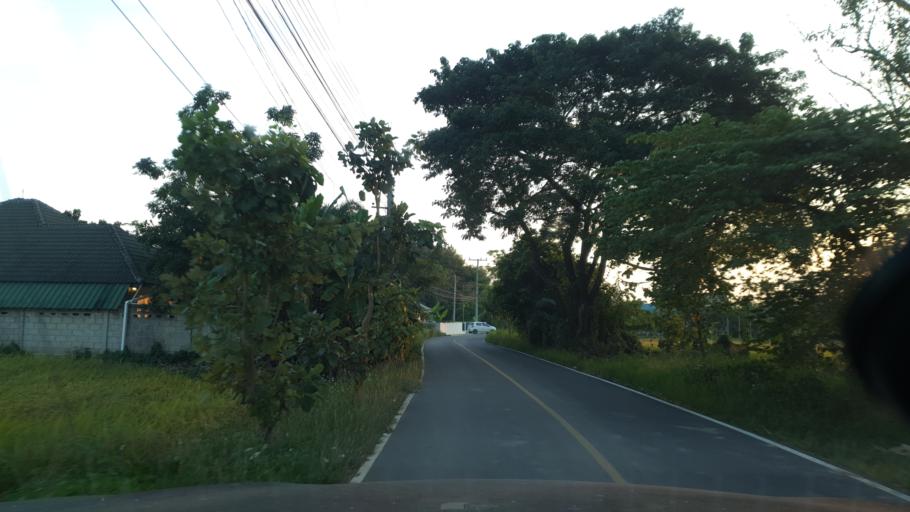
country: TH
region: Chiang Mai
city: San Sai
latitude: 18.8568
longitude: 99.0746
